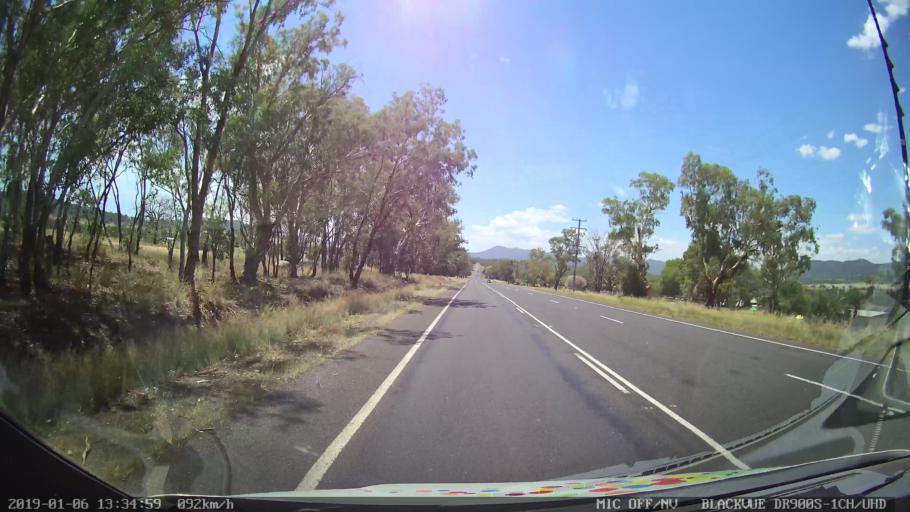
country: AU
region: New South Wales
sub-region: Tamworth Municipality
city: Kootingal
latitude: -31.0824
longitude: 151.0208
